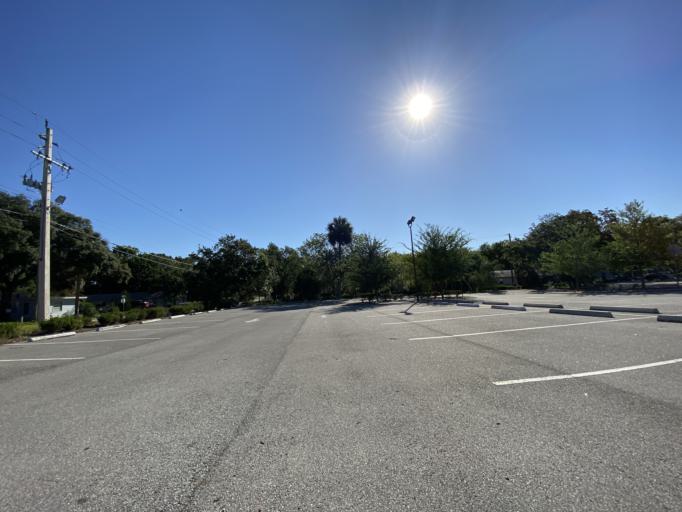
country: US
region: Florida
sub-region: Volusia County
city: Port Orange
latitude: 29.1440
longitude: -80.9905
